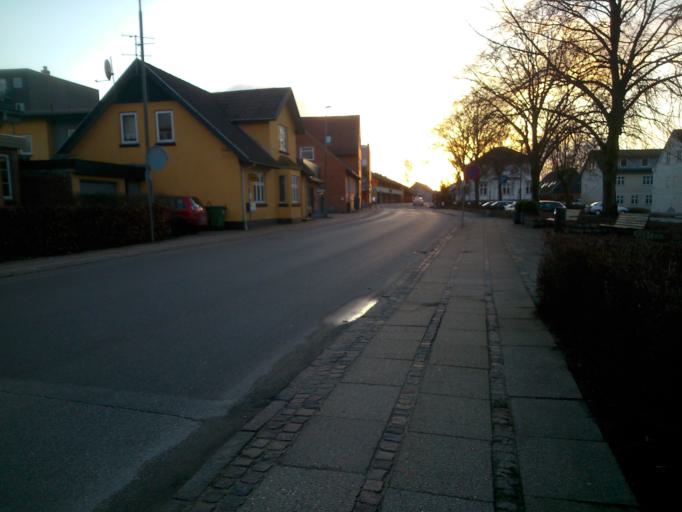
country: DK
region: Central Jutland
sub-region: Ikast-Brande Kommune
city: Ikast
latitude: 56.1433
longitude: 9.1559
